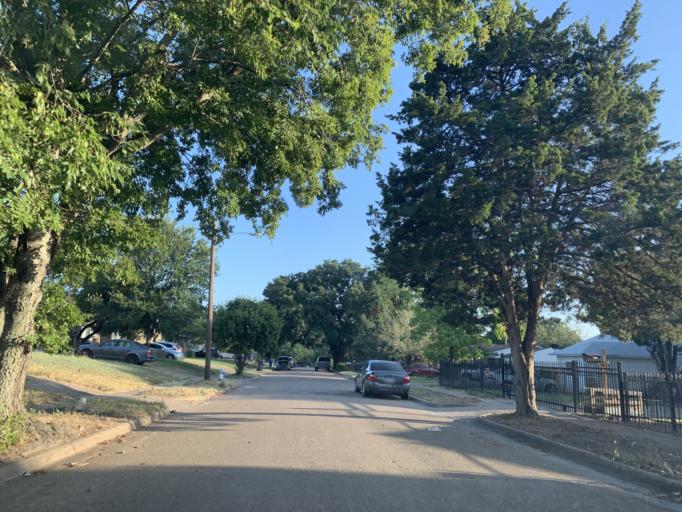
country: US
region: Texas
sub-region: Dallas County
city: Dallas
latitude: 32.7015
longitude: -96.8109
